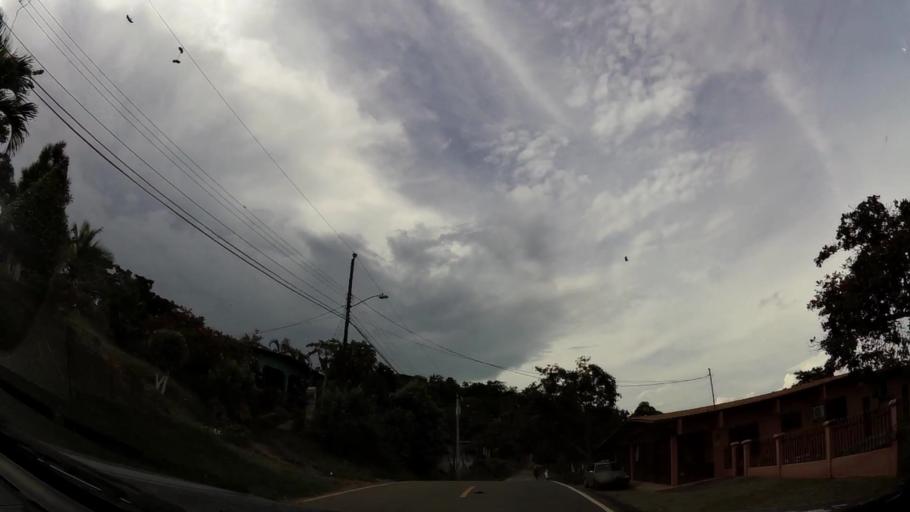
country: PA
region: Panama
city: Guadalupe
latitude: 8.8573
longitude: -79.8132
